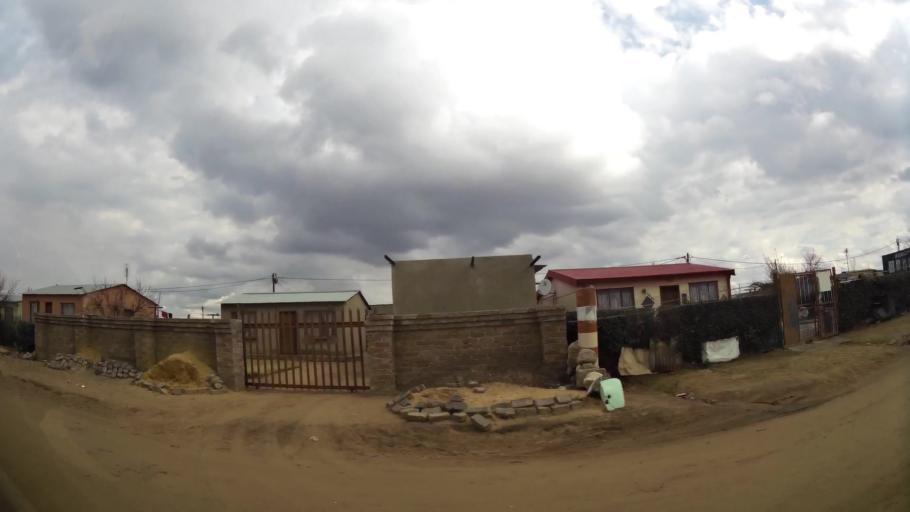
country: ZA
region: Orange Free State
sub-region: Fezile Dabi District Municipality
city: Sasolburg
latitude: -26.8664
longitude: 27.8683
